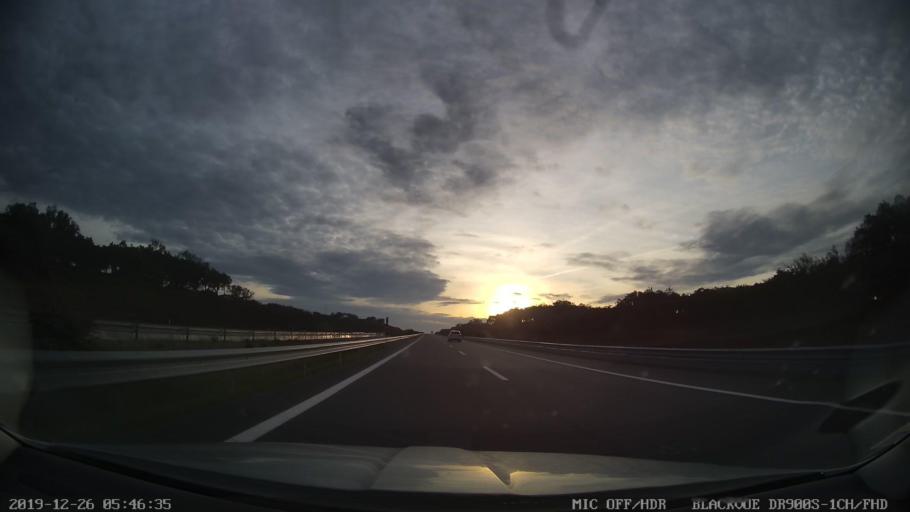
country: PT
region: Evora
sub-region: Estremoz
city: Estremoz
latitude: 38.7386
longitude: -7.7611
